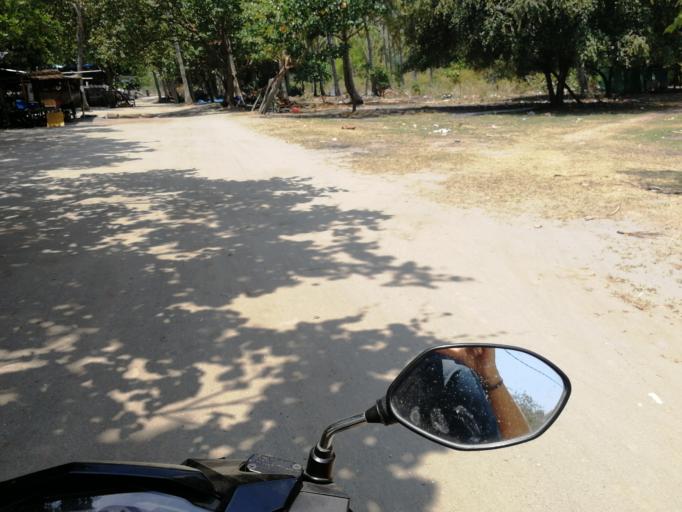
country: ID
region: West Nusa Tenggara
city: Karangsubagan
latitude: -8.4352
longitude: 116.0438
